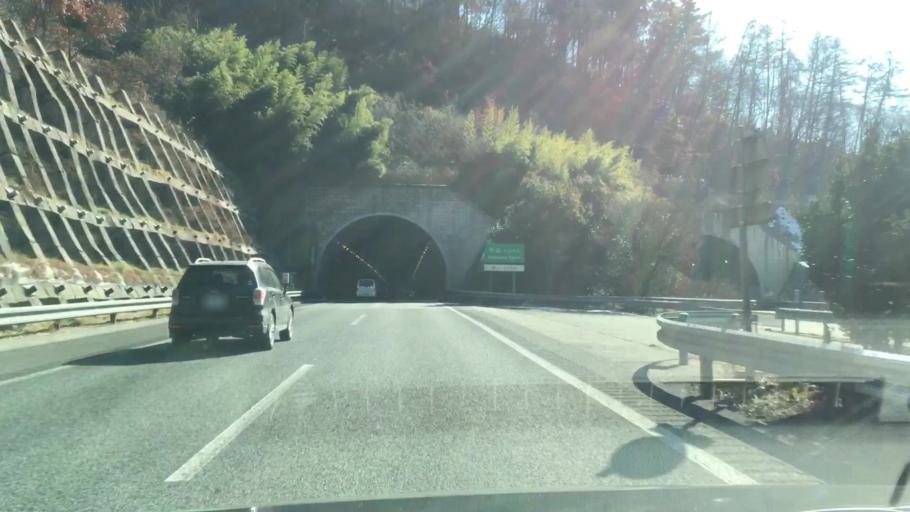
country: JP
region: Nagano
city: Ueda
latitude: 36.4776
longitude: 138.1925
